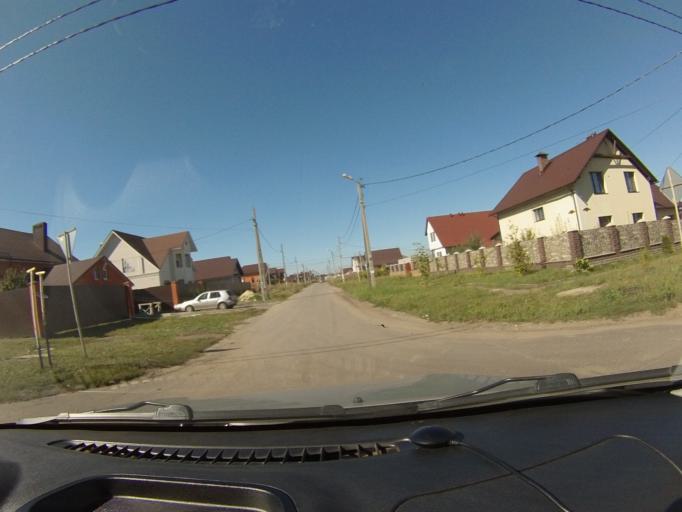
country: RU
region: Tambov
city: Tambov
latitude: 52.7755
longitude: 41.3731
